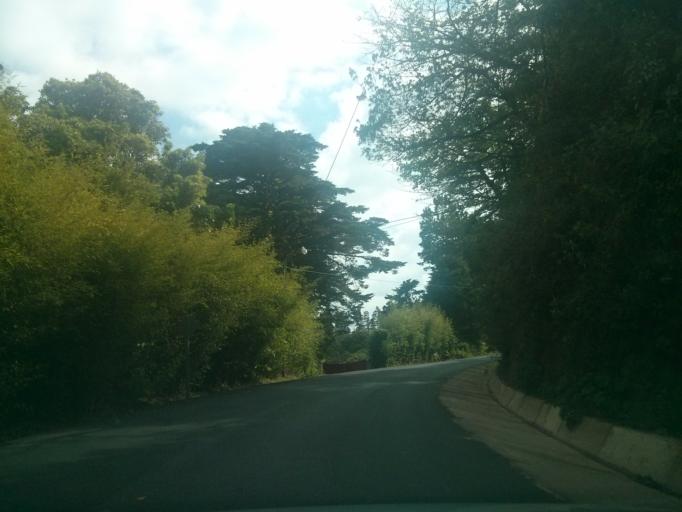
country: CR
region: Alajuela
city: Sabanilla
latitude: 10.1378
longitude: -84.1886
